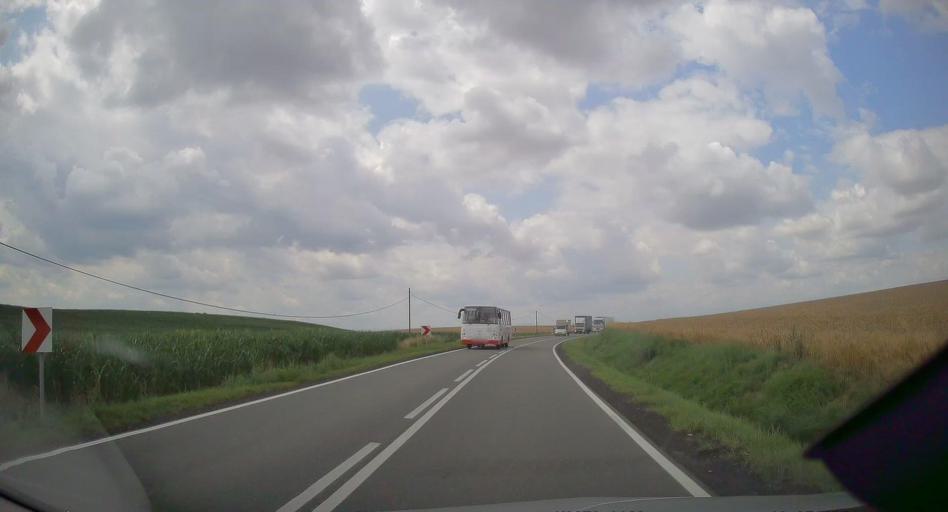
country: PL
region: Opole Voivodeship
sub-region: Powiat prudnicki
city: Glogowek
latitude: 50.3520
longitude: 17.8151
